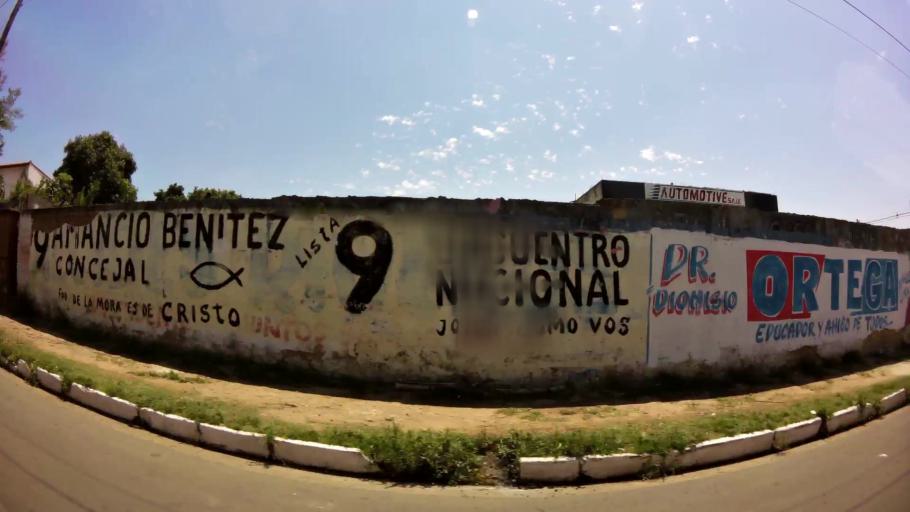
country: PY
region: Central
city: Fernando de la Mora
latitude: -25.3272
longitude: -57.5484
